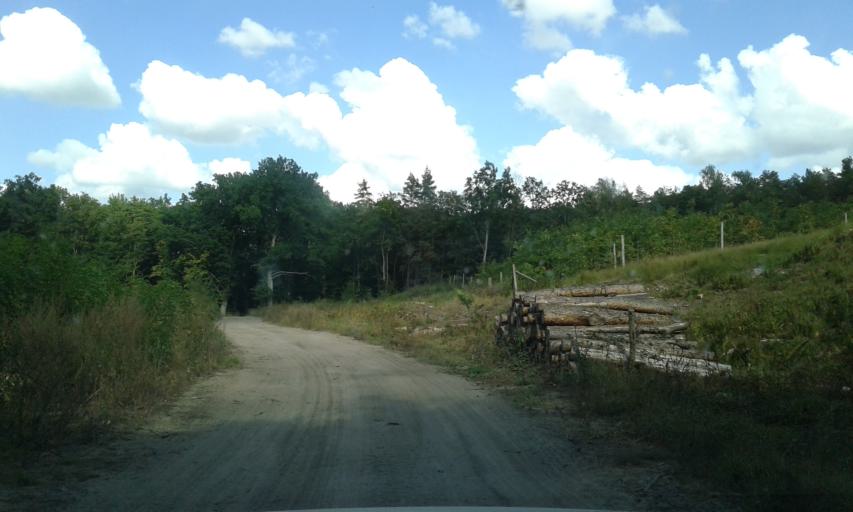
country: PL
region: West Pomeranian Voivodeship
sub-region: Powiat stargardzki
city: Dolice
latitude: 53.2481
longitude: 15.2251
